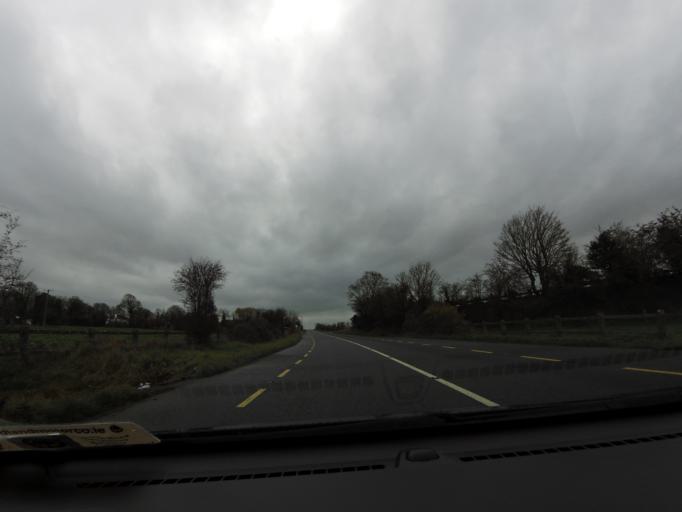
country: IE
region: Leinster
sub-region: Kilkenny
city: Ballyragget
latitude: 52.7658
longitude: -7.3326
